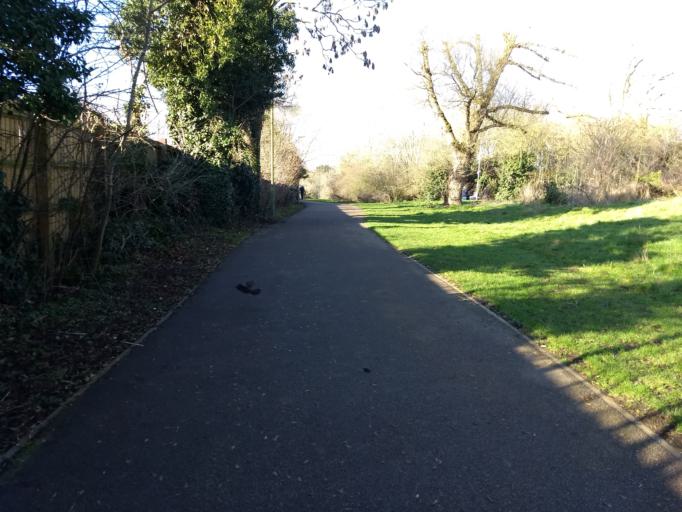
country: GB
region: England
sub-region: Buckinghamshire
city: Buckingham
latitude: 52.0001
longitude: -0.9806
